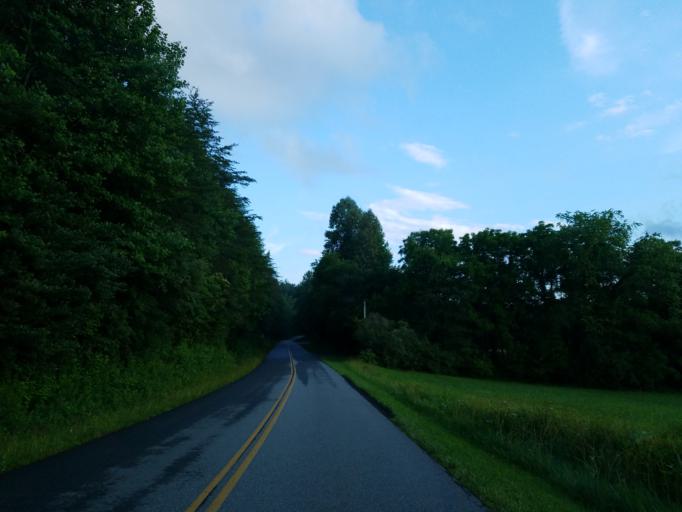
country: US
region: Georgia
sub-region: Fannin County
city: Blue Ridge
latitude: 34.7562
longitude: -84.2246
